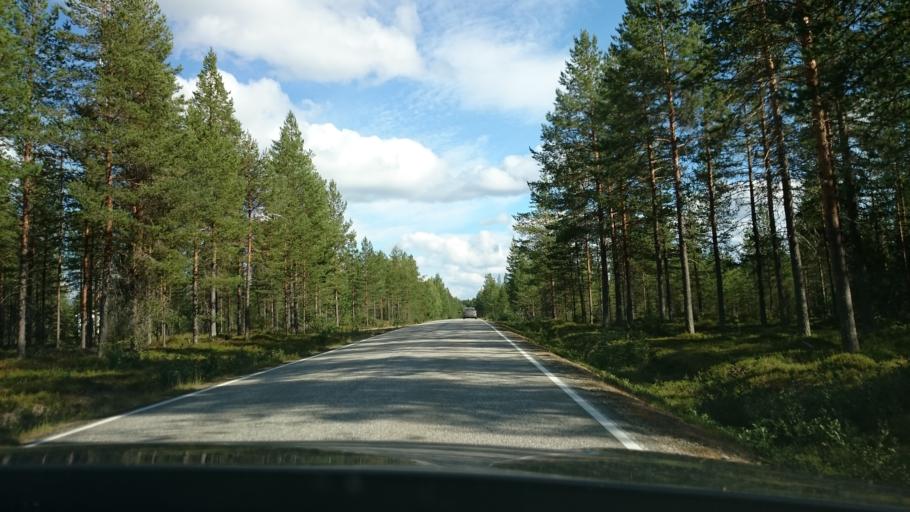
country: FI
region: Kainuu
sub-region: Kehys-Kainuu
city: Suomussalmi
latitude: 64.7510
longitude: 29.4242
